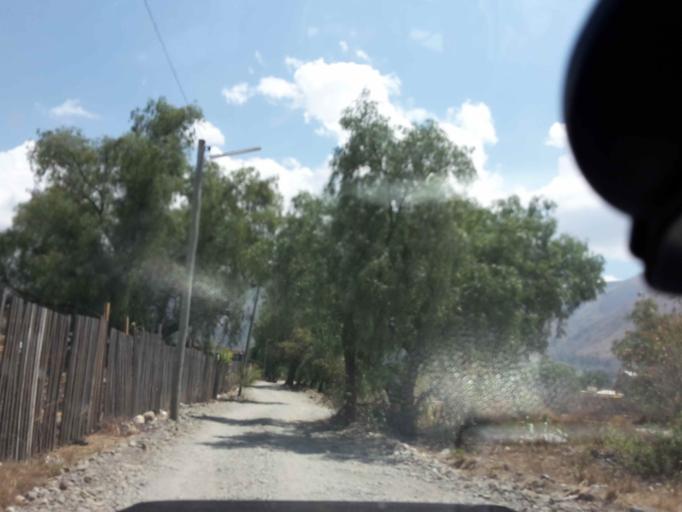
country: BO
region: Cochabamba
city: Cochabamba
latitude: -17.3434
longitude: -66.2124
